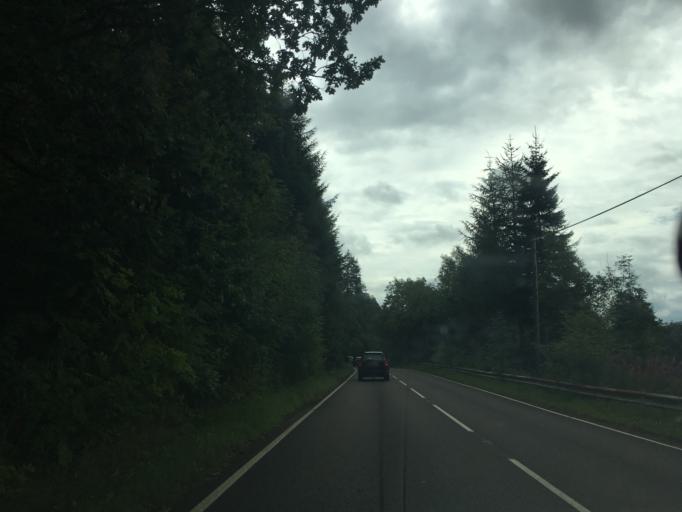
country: GB
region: Scotland
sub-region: Stirling
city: Callander
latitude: 56.2906
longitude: -4.2854
